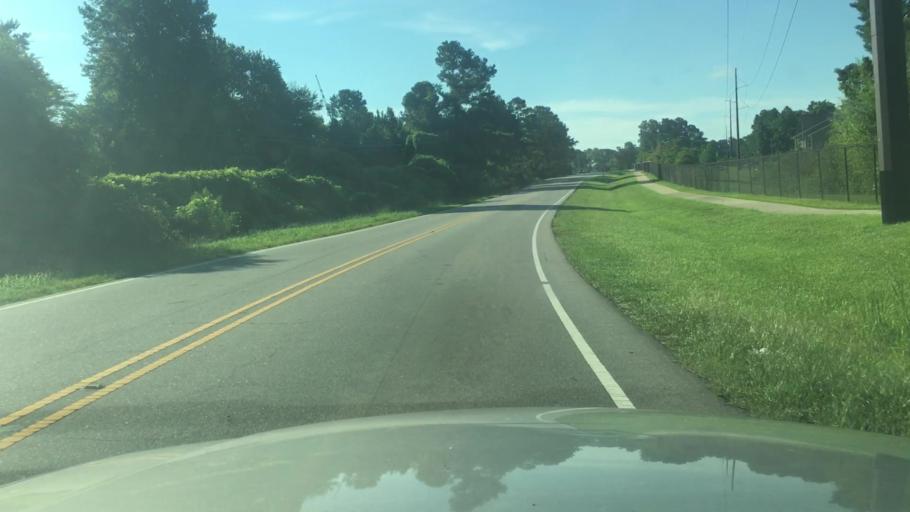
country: US
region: North Carolina
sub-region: Cumberland County
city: Fayetteville
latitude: 35.1256
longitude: -78.8887
